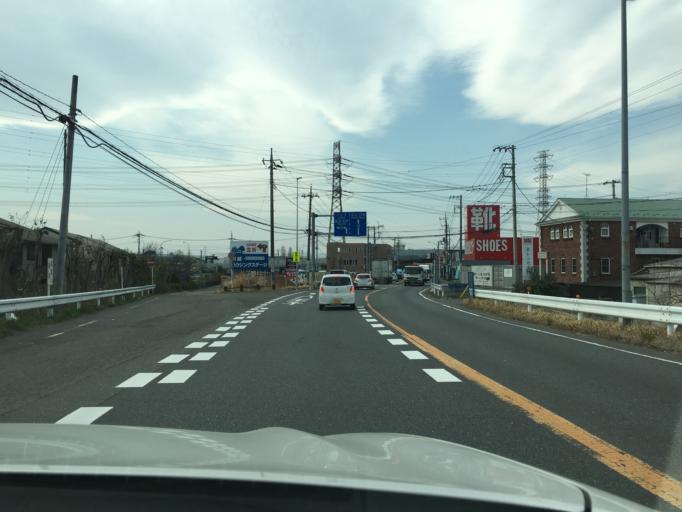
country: JP
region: Saitama
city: Kawagoe
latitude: 35.9171
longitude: 139.4689
